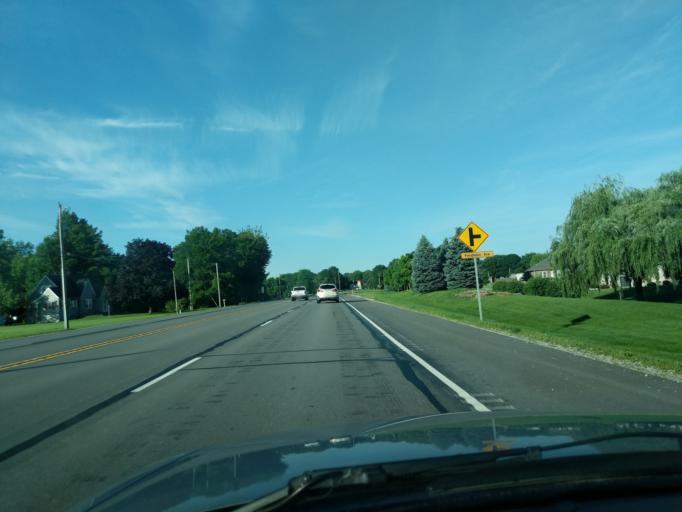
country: US
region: Indiana
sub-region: Madison County
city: Pendleton
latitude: 40.0296
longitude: -85.7275
